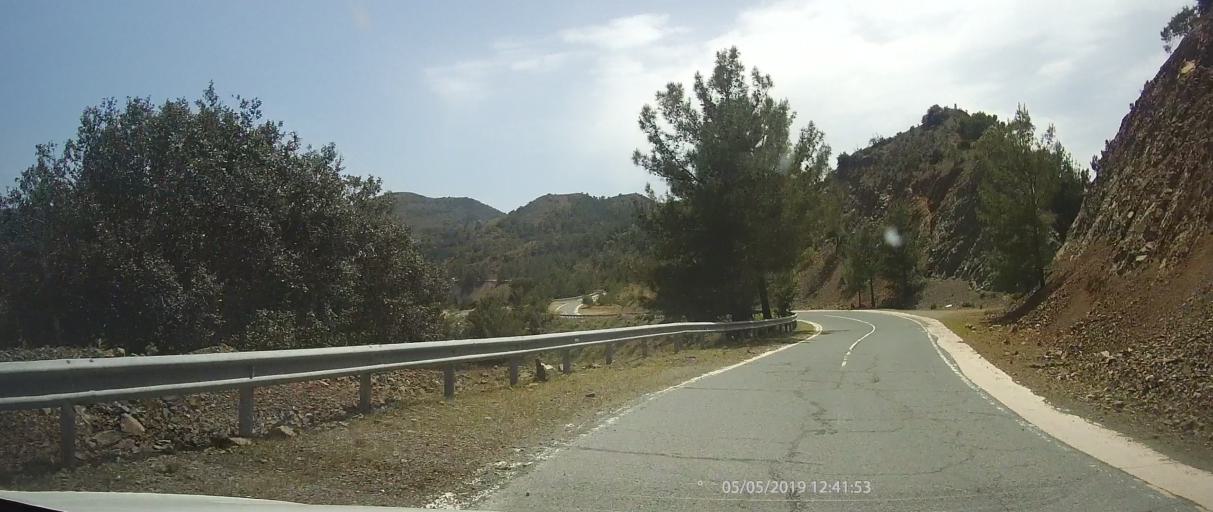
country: CY
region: Lefkosia
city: Kakopetria
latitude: 34.9786
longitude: 32.8098
